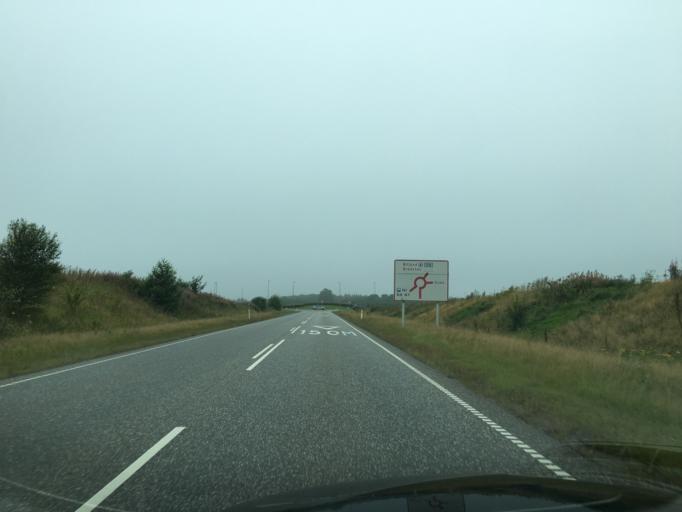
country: DK
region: South Denmark
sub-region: Kolding Kommune
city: Kolding
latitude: 55.5484
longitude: 9.4473
